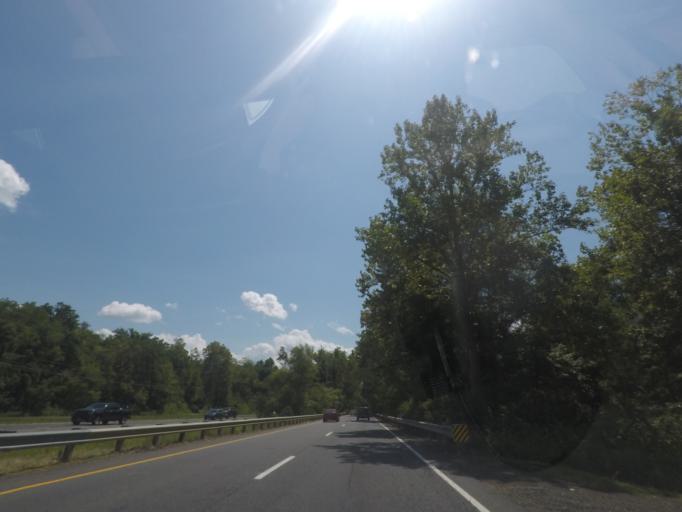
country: US
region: Virginia
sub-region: Fauquier County
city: Warrenton
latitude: 38.7781
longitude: -77.8251
